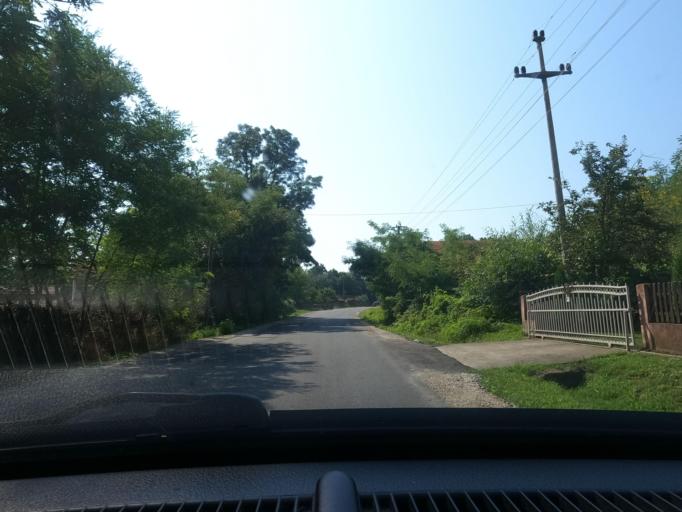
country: RS
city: Kozjak
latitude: 44.5646
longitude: 19.2895
